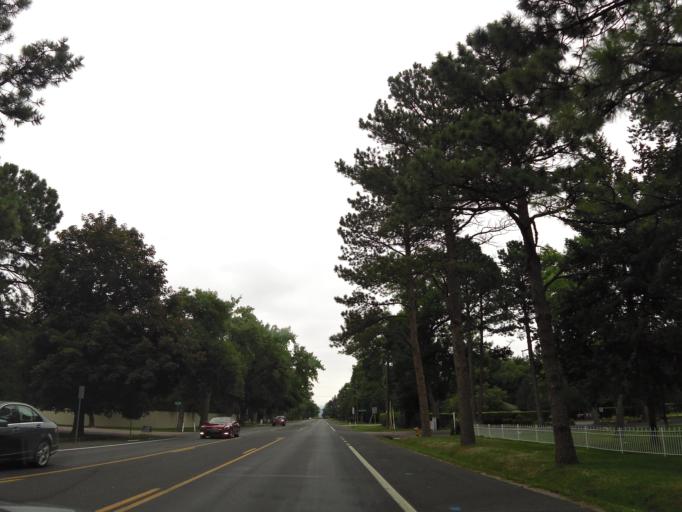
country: US
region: Colorado
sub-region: El Paso County
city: Colorado Springs
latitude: 38.7924
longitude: -104.8443
